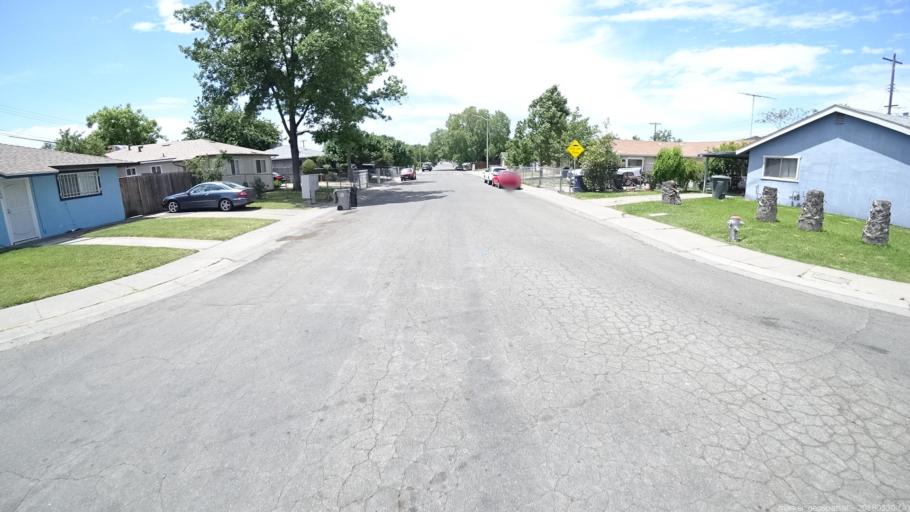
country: US
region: California
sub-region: Sacramento County
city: Sacramento
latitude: 38.6266
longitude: -121.4632
